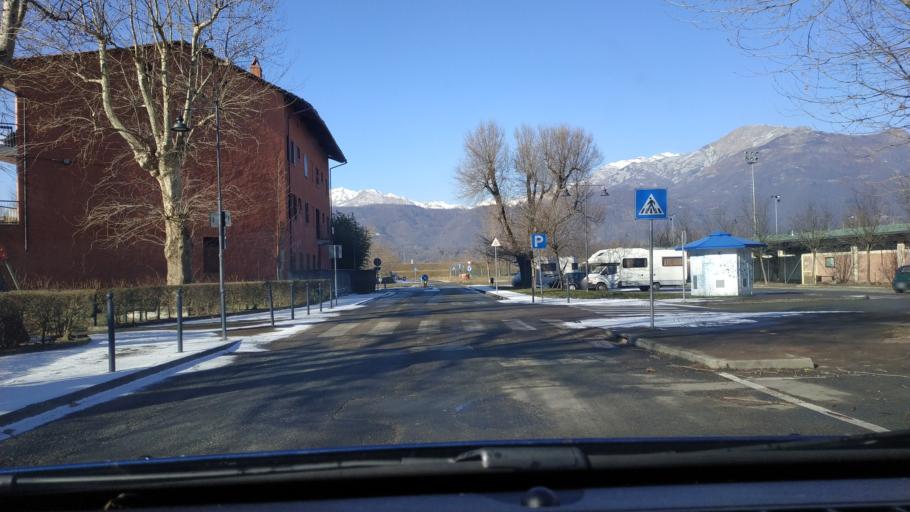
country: IT
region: Piedmont
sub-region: Provincia di Torino
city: Salerano Canavese
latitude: 45.4614
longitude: 7.8556
